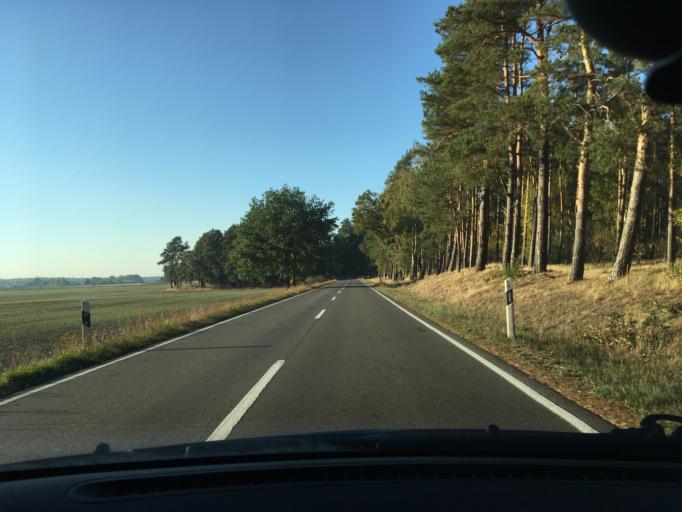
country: DE
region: Lower Saxony
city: Neu Darchau
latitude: 53.2698
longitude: 10.9480
